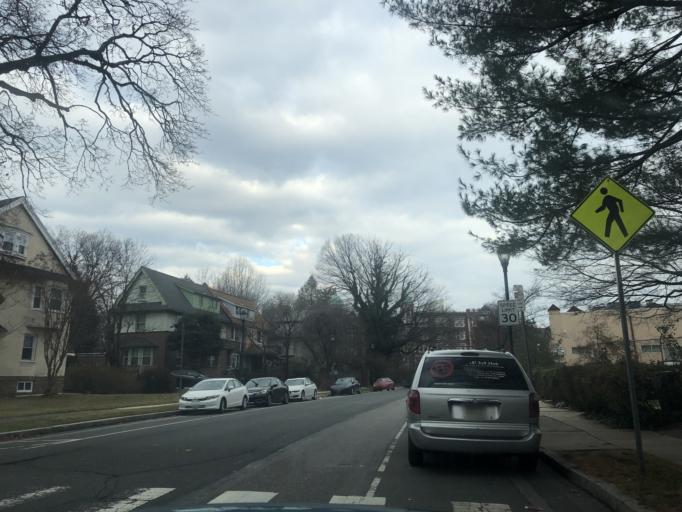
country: US
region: Pennsylvania
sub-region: Montgomery County
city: Narberth
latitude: 39.9874
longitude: -75.2491
